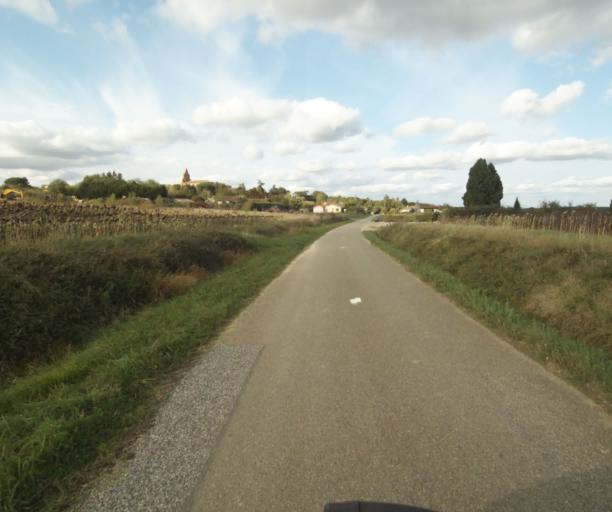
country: FR
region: Midi-Pyrenees
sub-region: Departement de la Haute-Garonne
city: Launac
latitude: 43.8392
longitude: 1.1208
